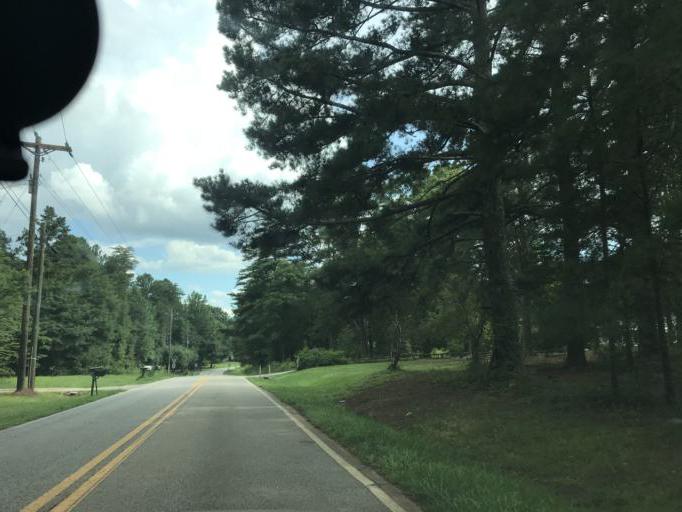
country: US
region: Georgia
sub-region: Forsyth County
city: Cumming
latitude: 34.2805
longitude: -84.1530
